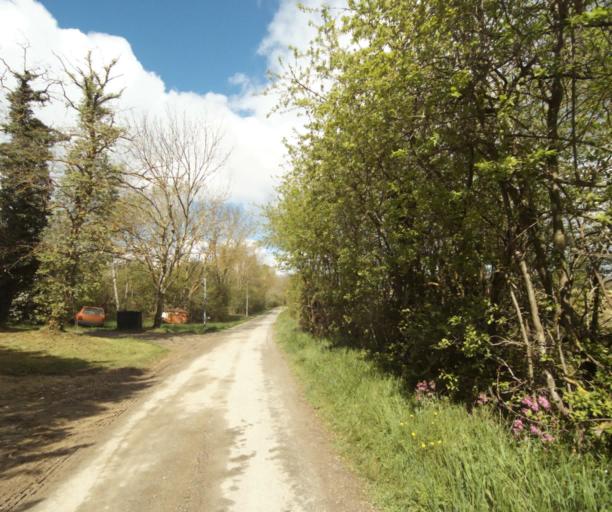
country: FR
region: Midi-Pyrenees
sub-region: Departement de l'Ariege
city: Saverdun
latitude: 43.1828
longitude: 1.5431
